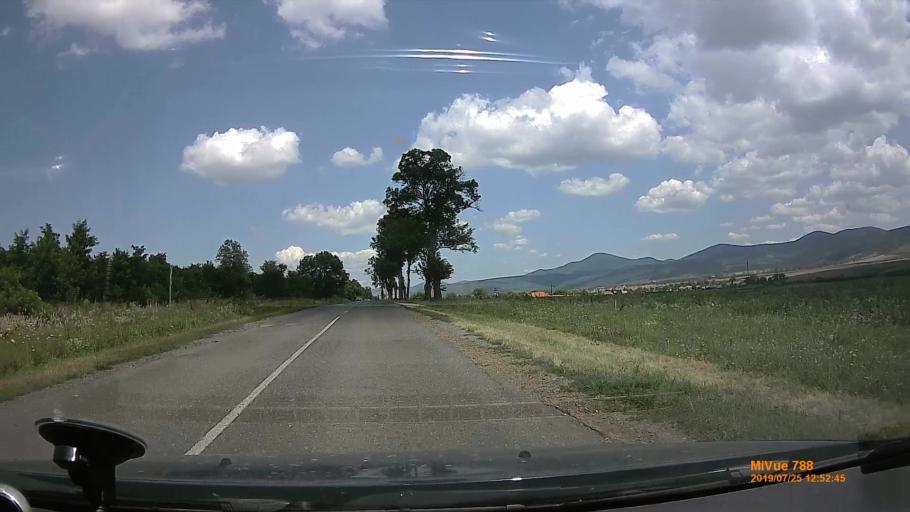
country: HU
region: Borsod-Abauj-Zemplen
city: Abaujszanto
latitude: 48.2943
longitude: 21.1911
